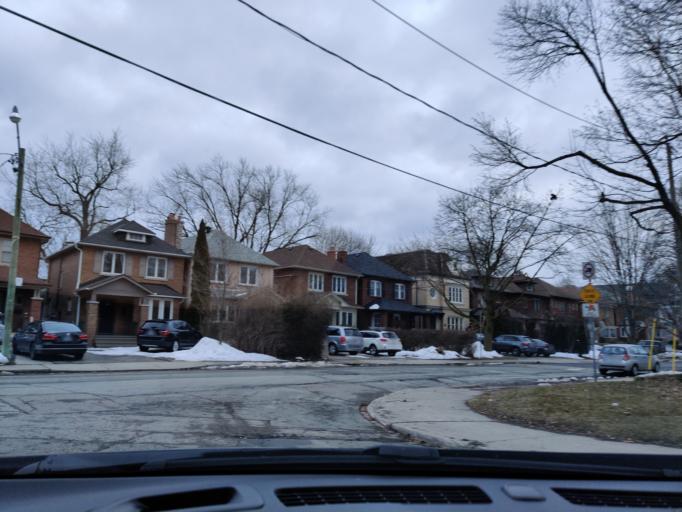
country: CA
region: Ontario
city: Willowdale
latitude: 43.7346
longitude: -79.4064
